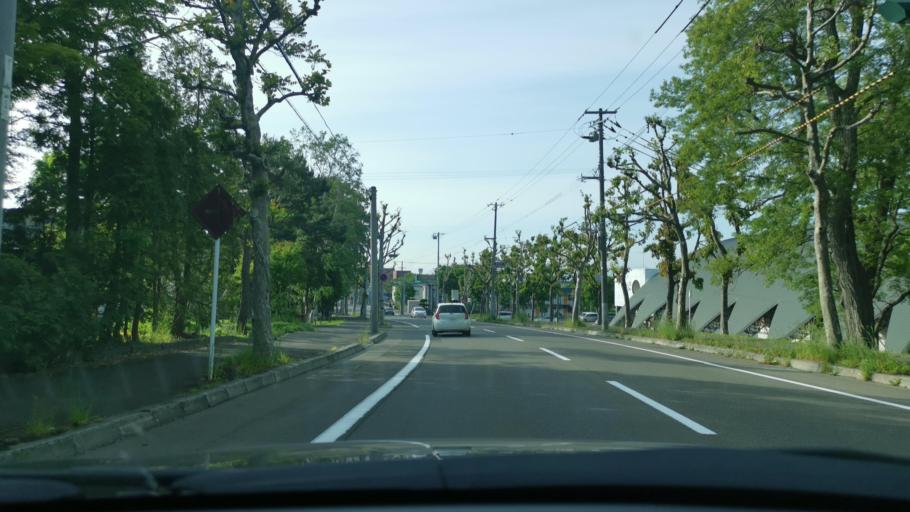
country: JP
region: Hokkaido
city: Iwamizawa
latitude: 43.1916
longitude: 141.7709
